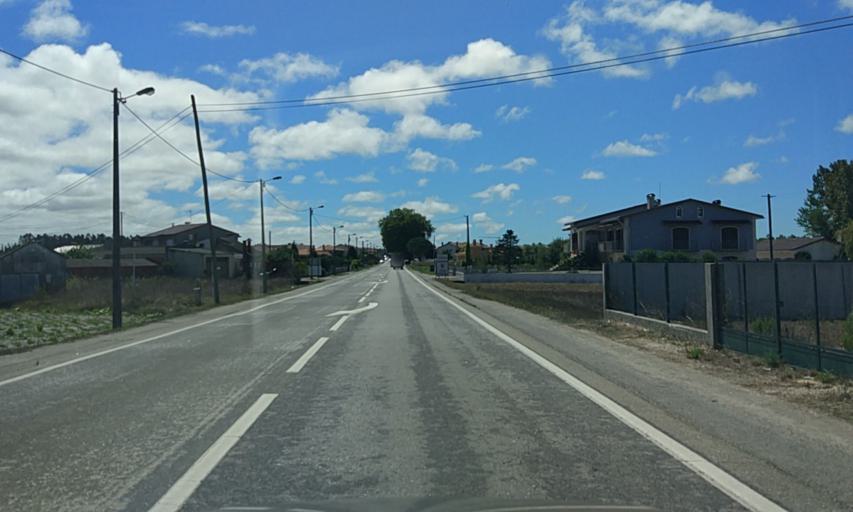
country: PT
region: Aveiro
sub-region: Vagos
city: Vagos
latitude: 40.4955
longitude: -8.6839
